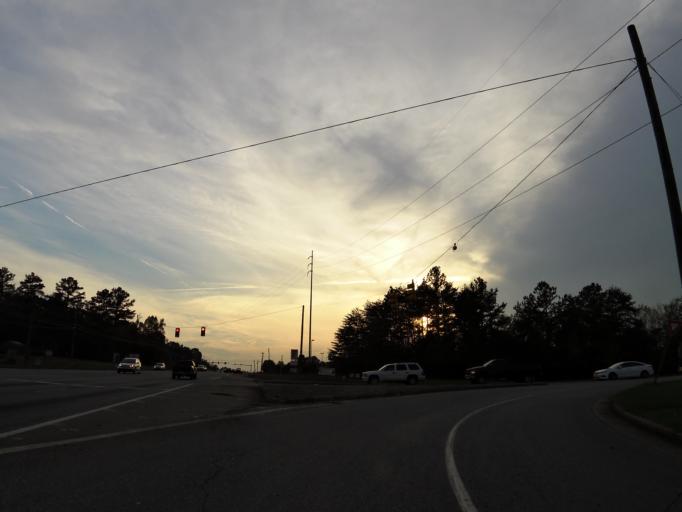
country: US
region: Tennessee
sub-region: Monroe County
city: Vonore
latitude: 35.5780
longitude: -84.2716
